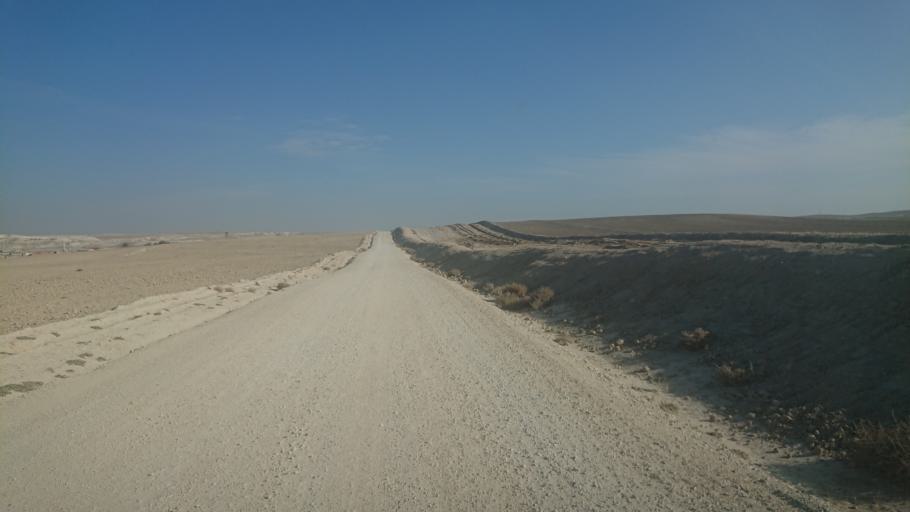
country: TR
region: Aksaray
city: Sultanhani
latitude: 38.0681
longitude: 33.6165
